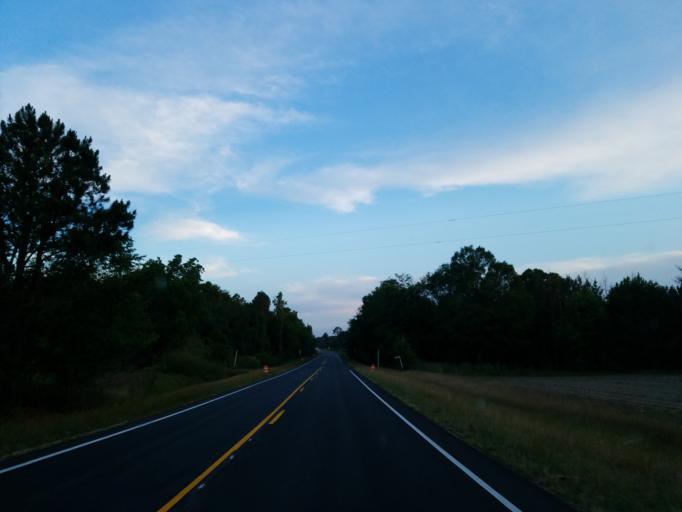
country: US
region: Georgia
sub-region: Turner County
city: Ashburn
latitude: 31.7674
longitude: -83.8080
